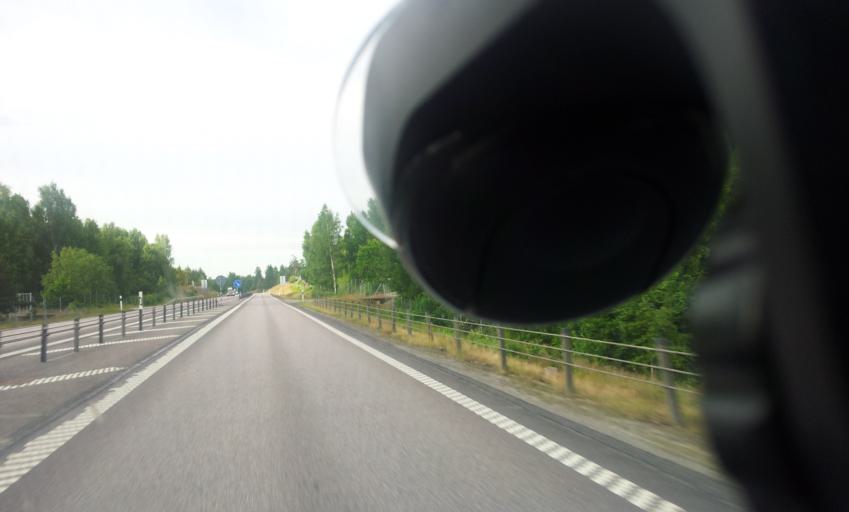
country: SE
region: Kalmar
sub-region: Oskarshamns Kommun
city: Oskarshamn
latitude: 57.2214
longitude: 16.4361
